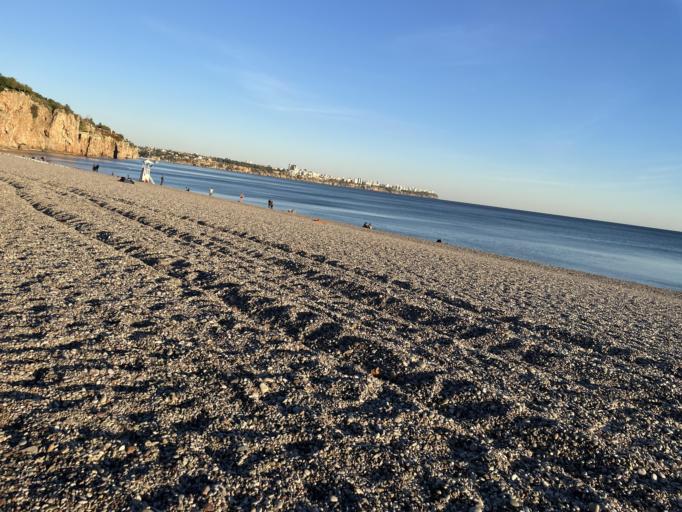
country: TR
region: Antalya
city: Antalya
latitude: 36.8831
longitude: 30.6755
